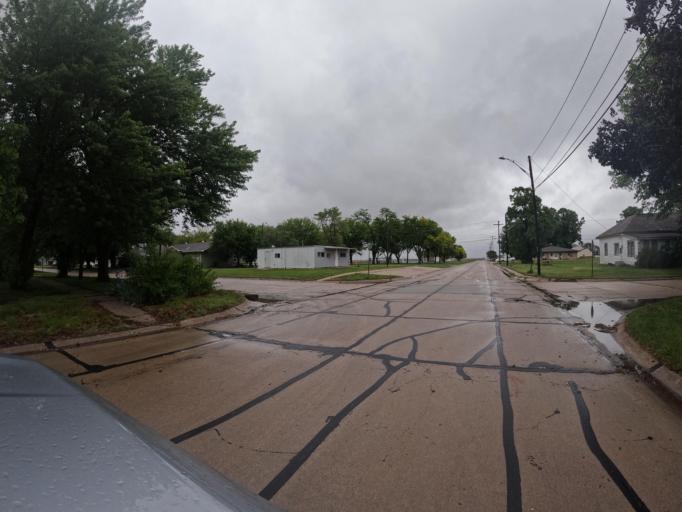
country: US
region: Nebraska
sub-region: Clay County
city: Harvard
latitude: 40.6189
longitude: -98.0933
